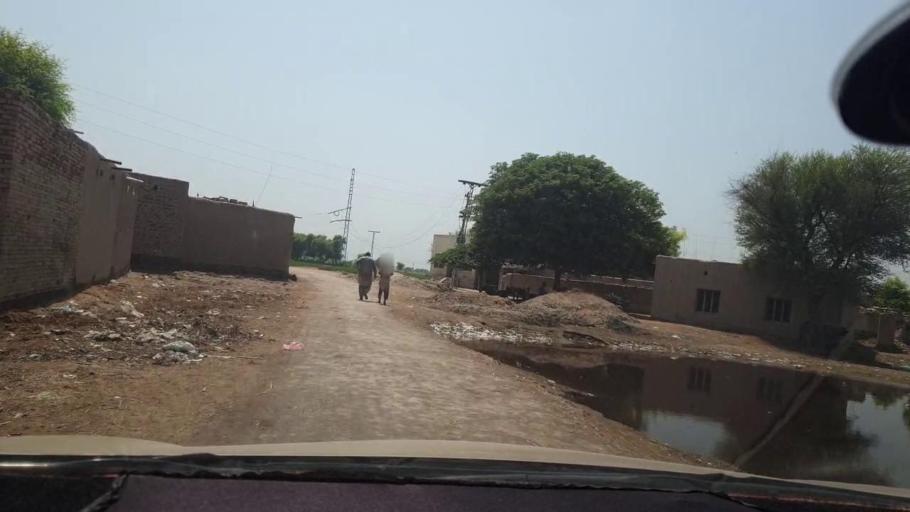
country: PK
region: Sindh
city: Kambar
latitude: 27.6340
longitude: 67.9326
